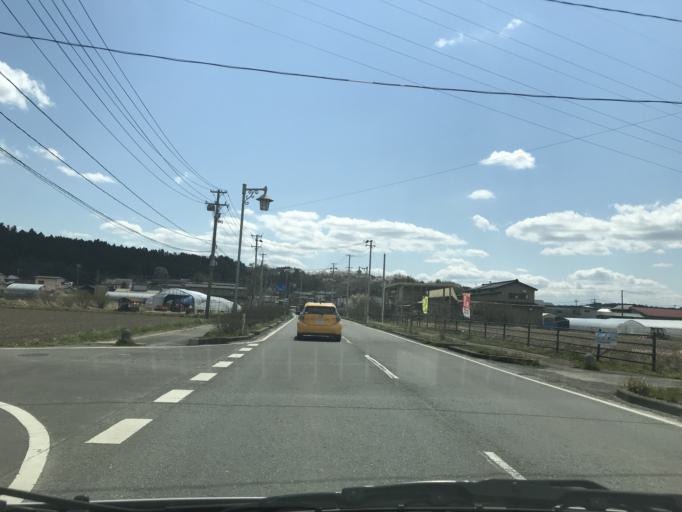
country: JP
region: Miyagi
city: Wakuya
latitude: 38.6535
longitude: 141.2727
